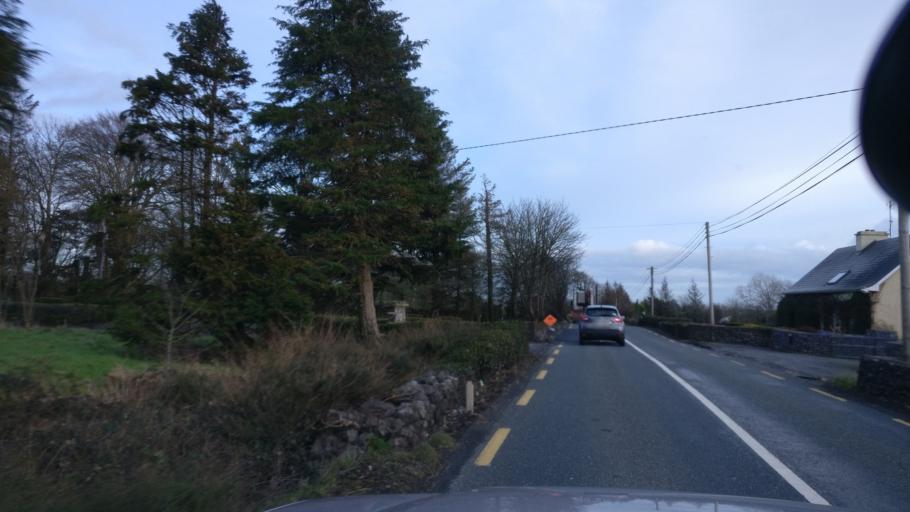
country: IE
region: Connaught
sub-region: County Galway
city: Moycullen
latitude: 53.4876
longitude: -9.1247
